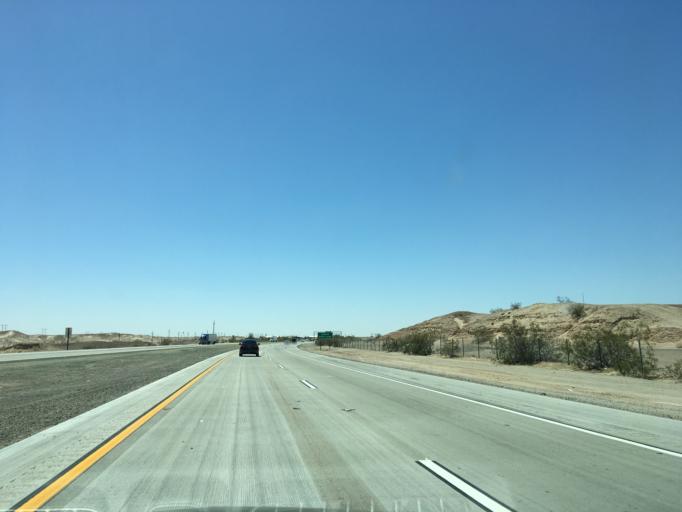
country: MX
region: Baja California
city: Los Algodones
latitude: 32.7447
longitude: -114.7294
